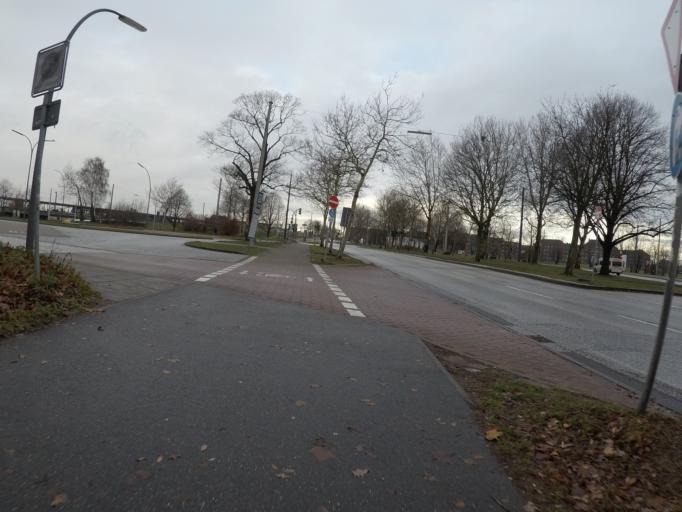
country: DE
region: Hamburg
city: Kleiner Grasbrook
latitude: 53.5203
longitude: 10.0153
